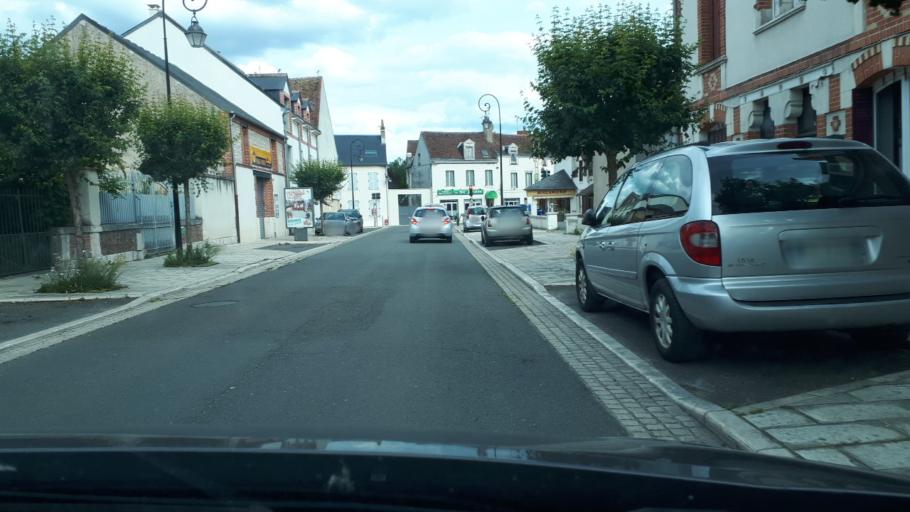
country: FR
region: Centre
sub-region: Departement du Loir-et-Cher
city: Romorantin-Lanthenay
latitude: 47.3550
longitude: 1.7416
